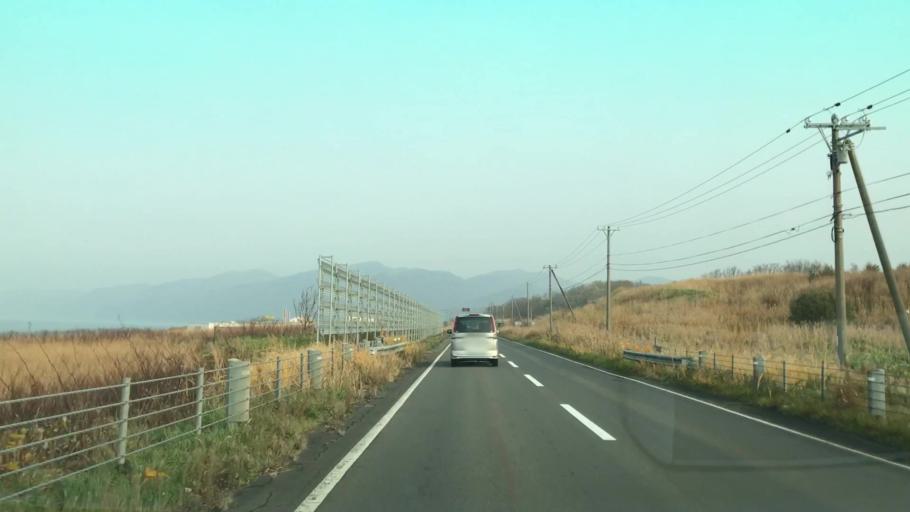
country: JP
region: Hokkaido
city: Ishikari
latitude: 43.3725
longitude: 141.4269
